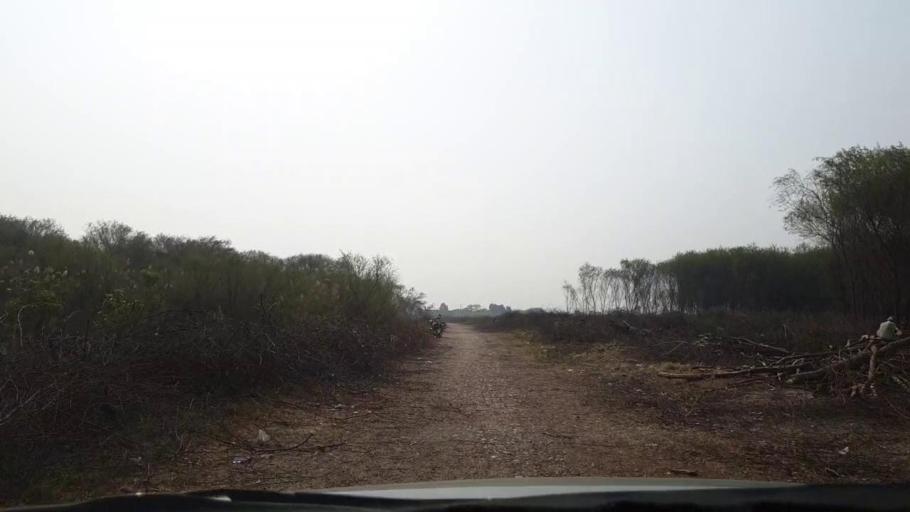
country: PK
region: Sindh
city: Matiari
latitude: 25.6362
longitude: 68.5156
